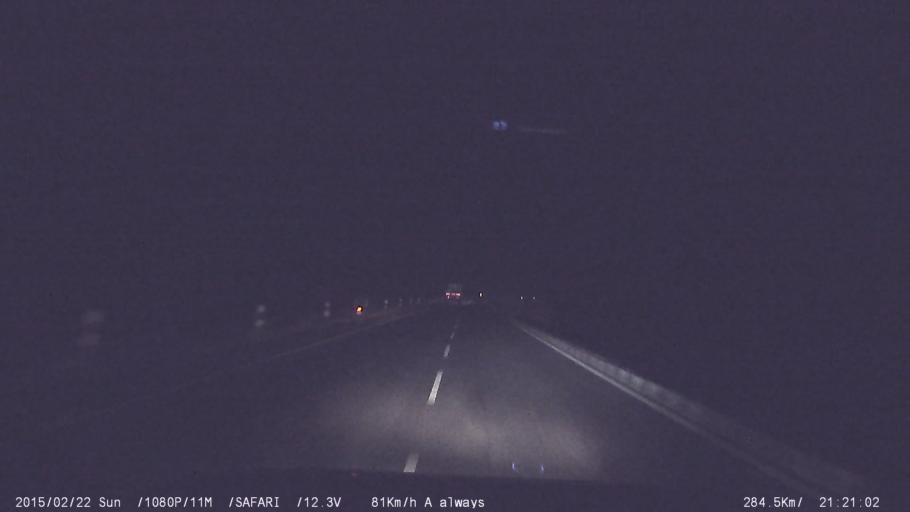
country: IN
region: Tamil Nadu
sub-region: Karur
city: Karur
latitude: 10.8602
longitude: 77.9874
